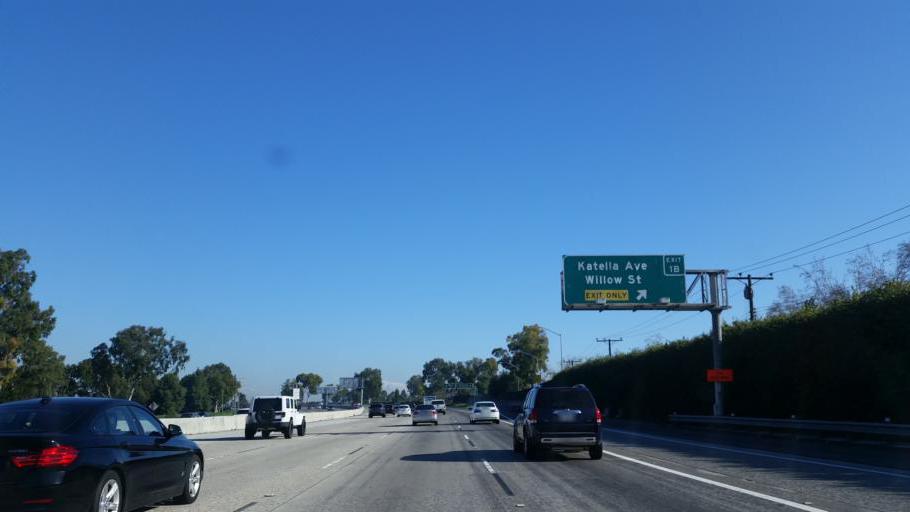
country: US
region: California
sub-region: Orange County
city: Los Alamitos
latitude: 33.7996
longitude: -118.0841
